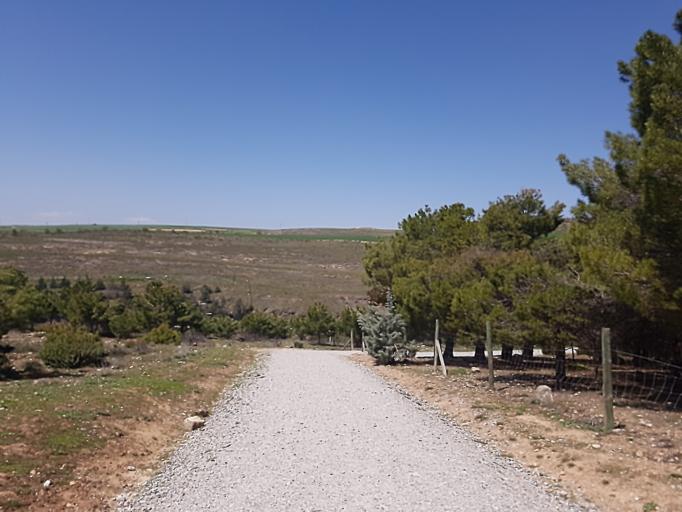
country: ES
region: Castille and Leon
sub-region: Provincia de Segovia
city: Segovia
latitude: 40.9535
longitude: -4.1359
